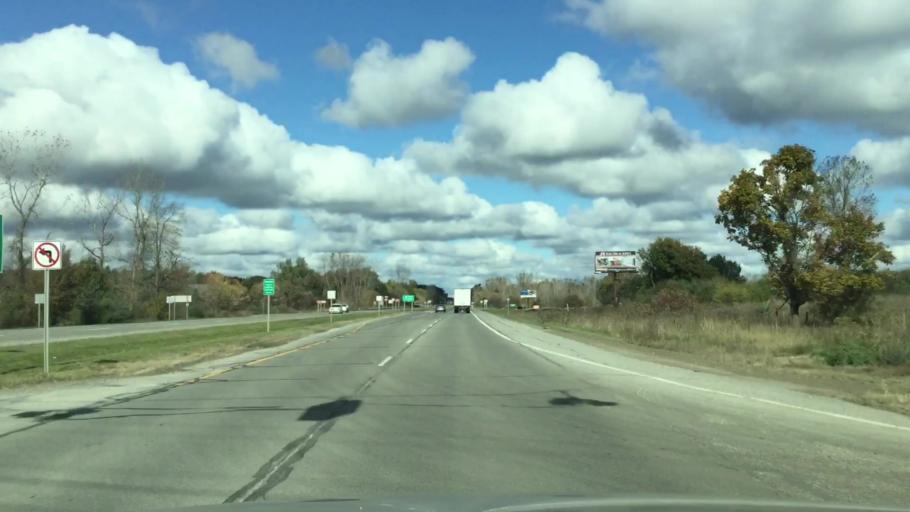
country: US
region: Michigan
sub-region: Oakland County
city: Oxford
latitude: 42.8691
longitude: -83.2955
